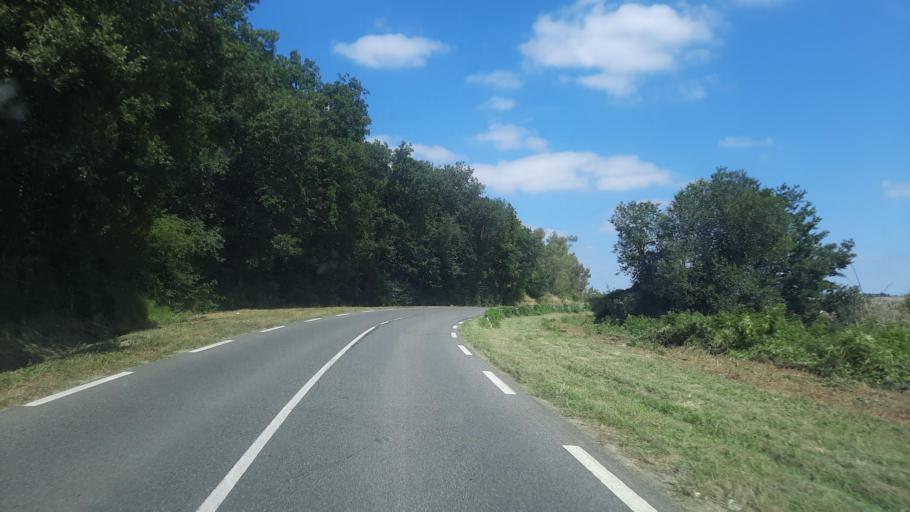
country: FR
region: Midi-Pyrenees
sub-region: Departement du Gers
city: Lombez
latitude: 43.4480
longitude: 0.8648
